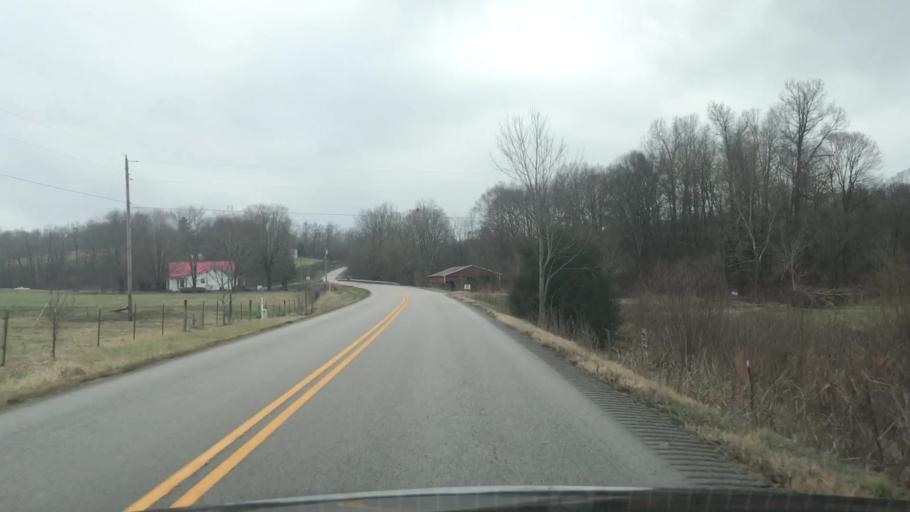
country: US
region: Kentucky
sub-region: Monroe County
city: Tompkinsville
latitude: 36.8538
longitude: -85.7718
